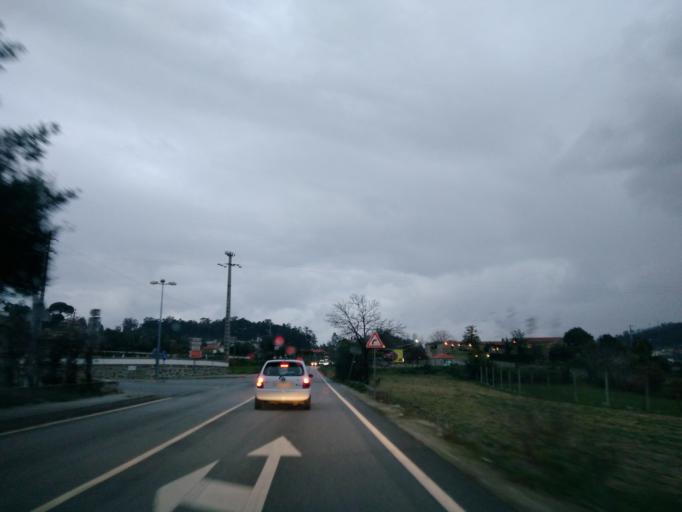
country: PT
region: Braga
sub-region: Braga
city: Oliveira
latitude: 41.4811
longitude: -8.4807
